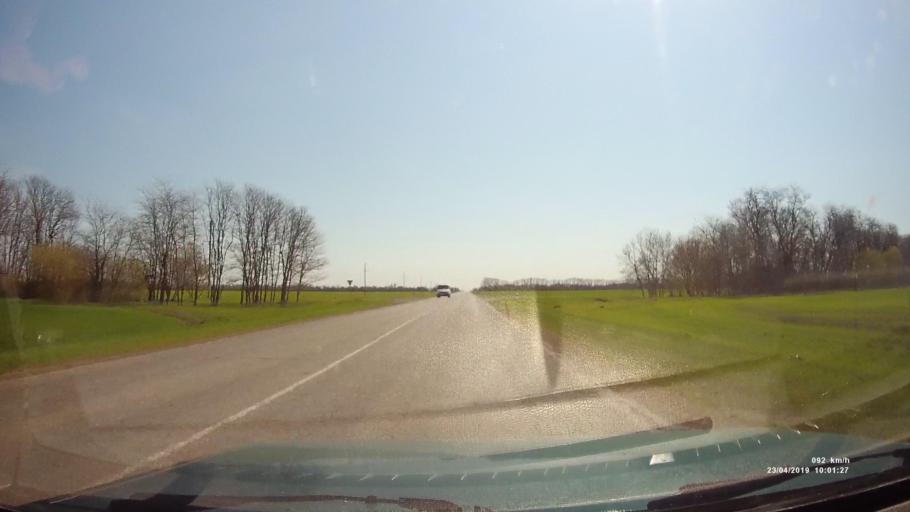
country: RU
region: Rostov
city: Sovetskoye
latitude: 46.7655
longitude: 42.1504
